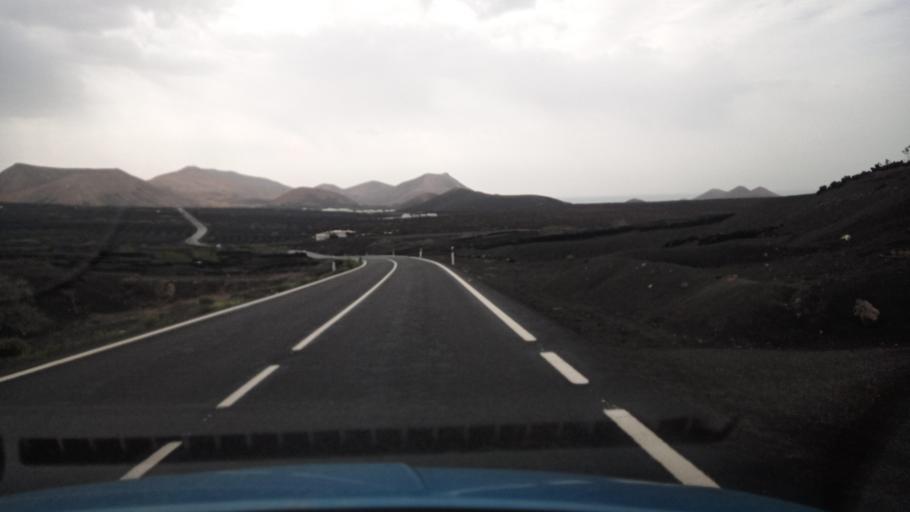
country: ES
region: Canary Islands
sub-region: Provincia de Las Palmas
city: Yaiza
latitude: 28.9639
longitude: -13.7245
